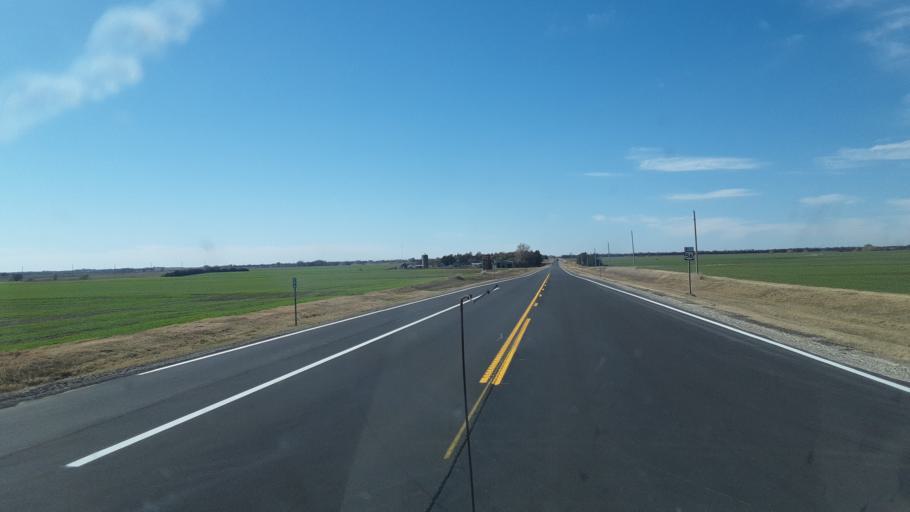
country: US
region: Kansas
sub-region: Rice County
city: Lyons
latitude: 38.3766
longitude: -98.0904
